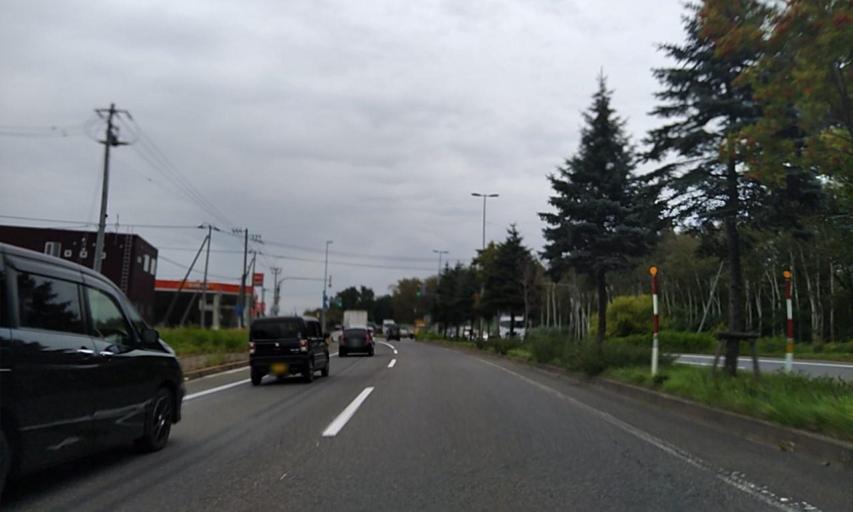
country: JP
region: Hokkaido
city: Ishikari
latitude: 43.1595
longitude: 141.2802
